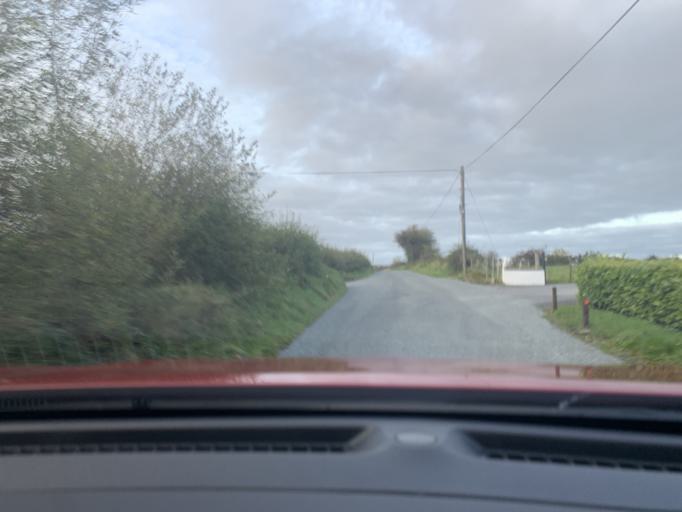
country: IE
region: Connaught
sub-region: Roscommon
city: Ballaghaderreen
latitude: 53.9819
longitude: -8.6160
